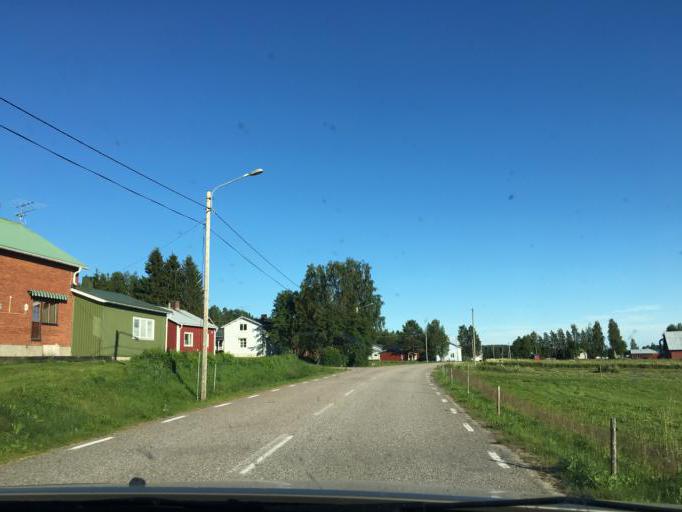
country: SE
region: Norrbotten
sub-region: Kalix Kommun
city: Rolfs
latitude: 65.9010
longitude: 22.9337
